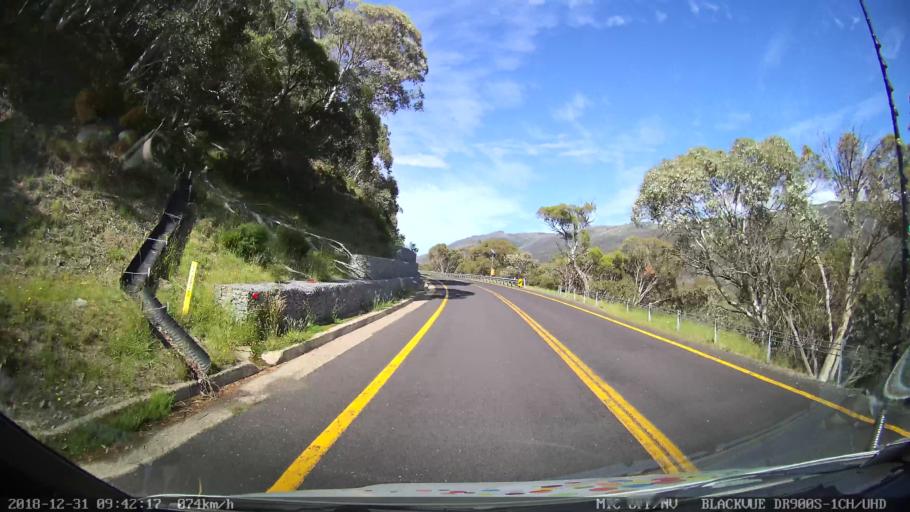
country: AU
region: New South Wales
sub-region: Snowy River
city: Jindabyne
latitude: -36.4956
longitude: 148.3248
